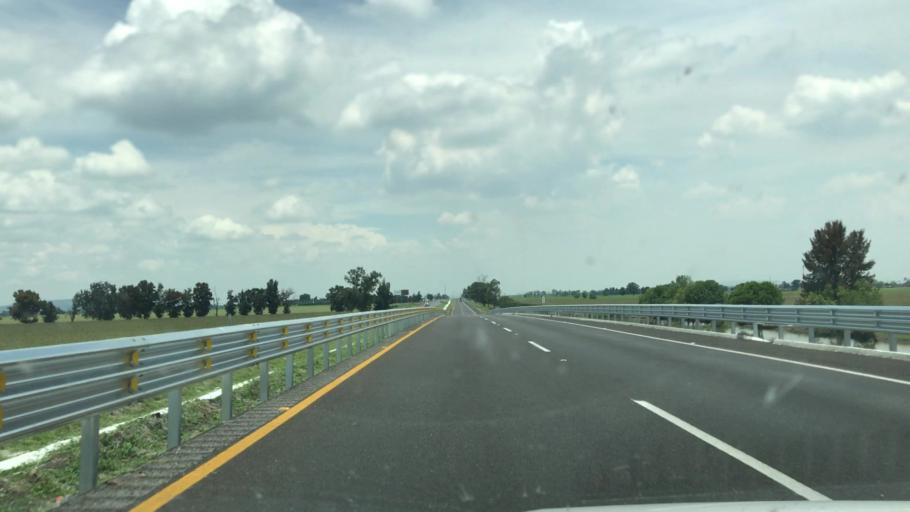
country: MX
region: Guanajuato
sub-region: Salamanca
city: San Vicente de Flores
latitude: 20.6358
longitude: -101.2582
